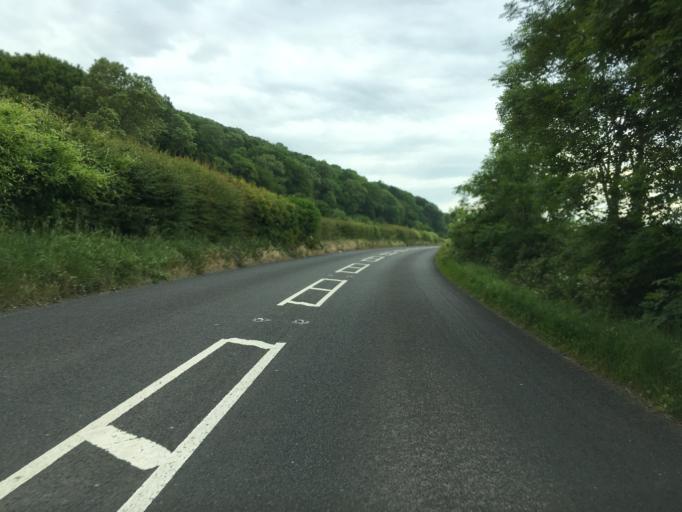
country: GB
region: England
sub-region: North Somerset
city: Clevedon
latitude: 51.4564
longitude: -2.8239
